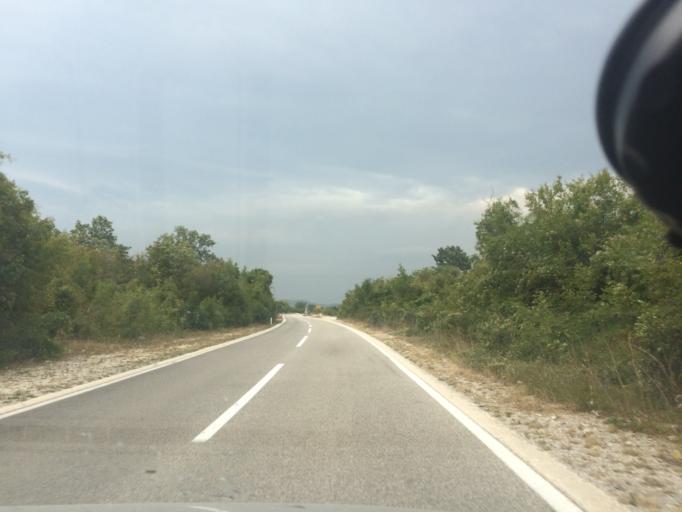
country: ME
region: Kotor
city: Risan
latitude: 42.5817
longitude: 18.6871
